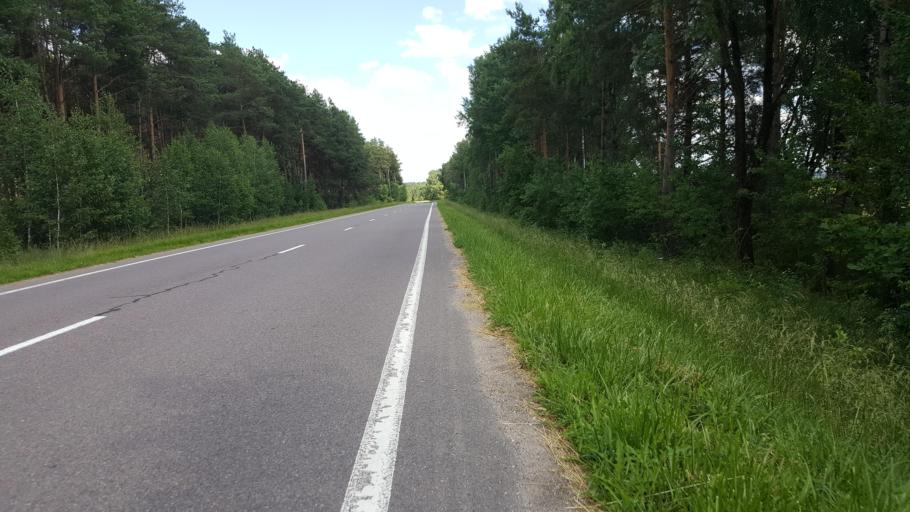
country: BY
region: Brest
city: Kamyanyuki
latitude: 52.5036
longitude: 23.6816
